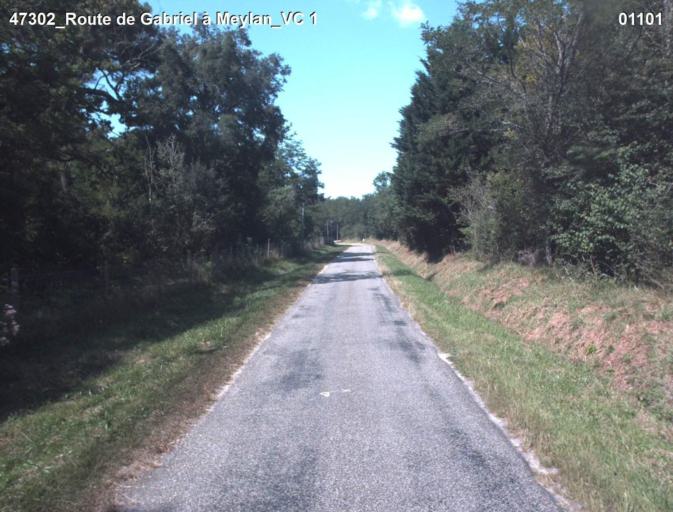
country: FR
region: Aquitaine
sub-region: Departement du Lot-et-Garonne
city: Mezin
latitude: 44.0616
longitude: 0.1434
